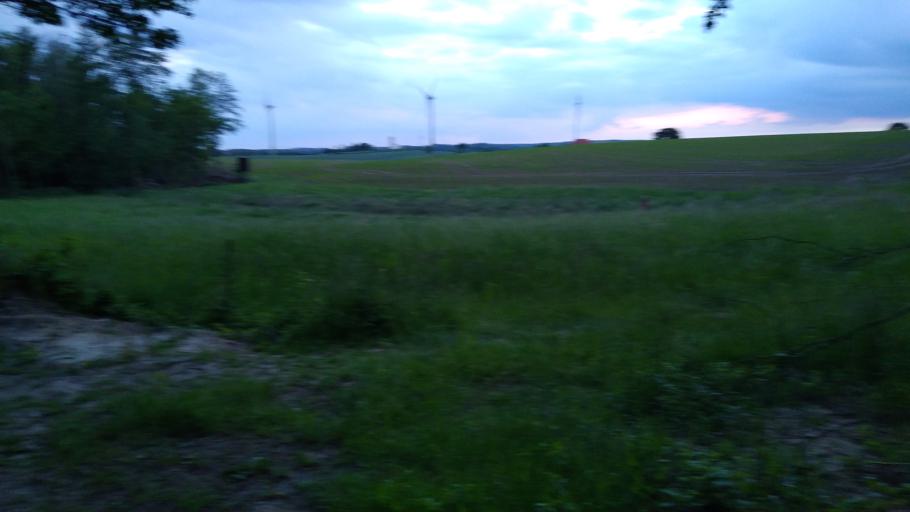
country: DE
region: Schleswig-Holstein
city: Kabelhorst
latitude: 54.2308
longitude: 10.9141
